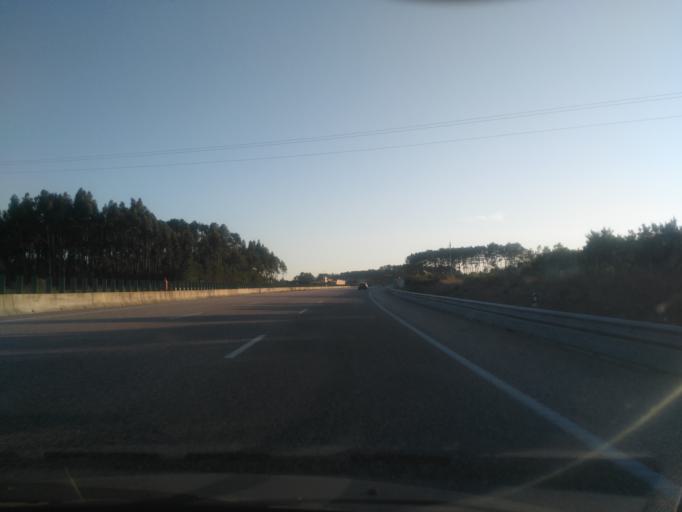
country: PT
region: Leiria
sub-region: Leiria
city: Monte Redondo
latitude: 39.9350
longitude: -8.7736
